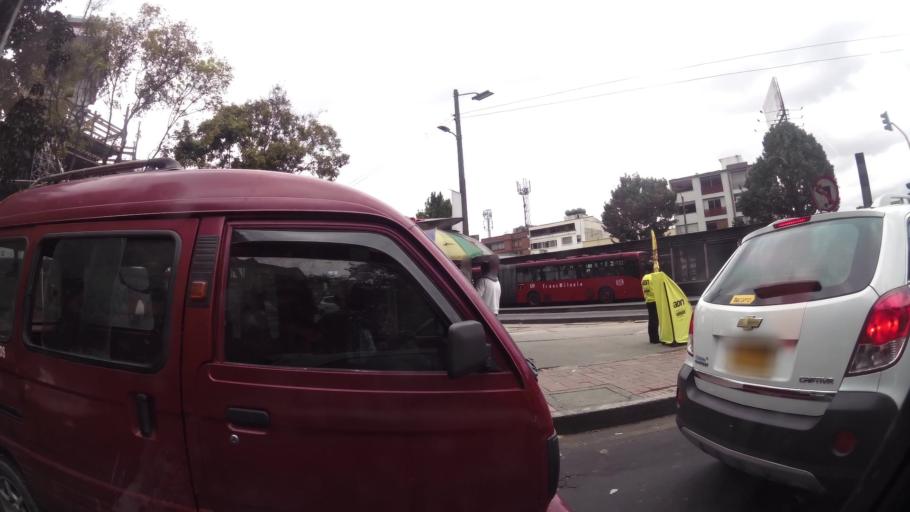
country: CO
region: Bogota D.C.
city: Bogota
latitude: 4.6171
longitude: -74.0717
